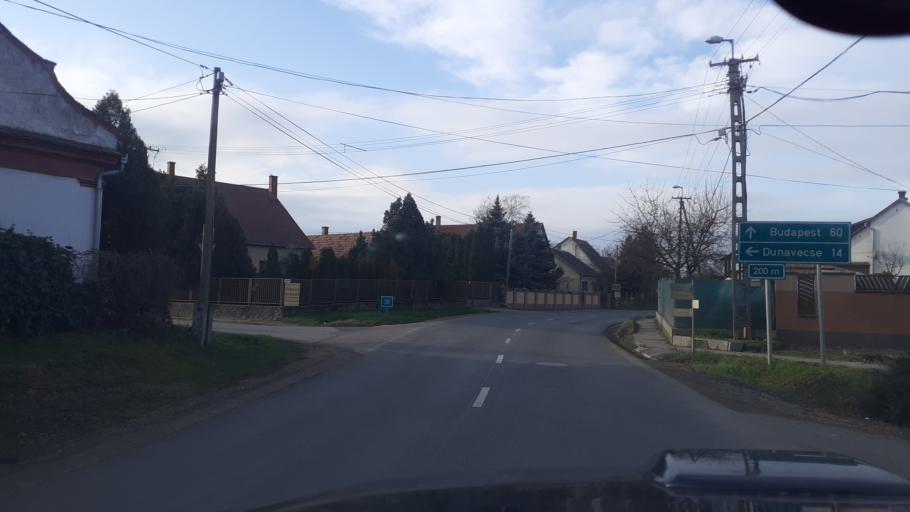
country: HU
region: Bacs-Kiskun
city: Tass
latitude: 47.0190
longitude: 19.0364
